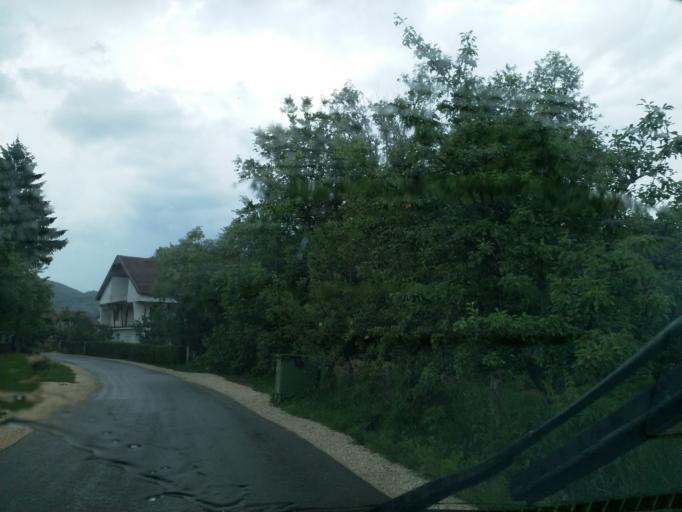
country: RS
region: Central Serbia
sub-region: Borski Okrug
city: Bor
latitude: 44.0121
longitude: 21.9845
